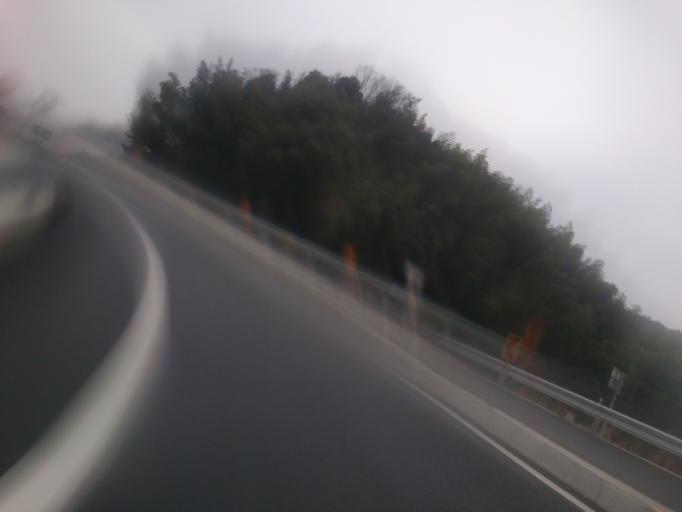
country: JP
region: Kyoto
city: Miyazu
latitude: 35.5509
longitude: 135.1445
